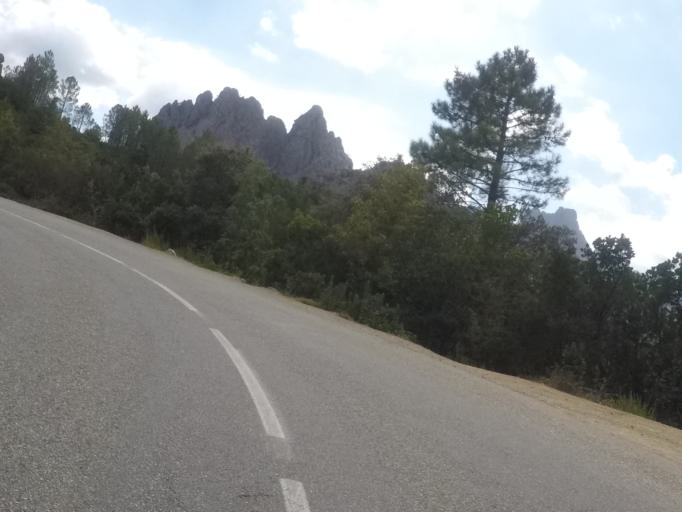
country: FR
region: Corsica
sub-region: Departement de la Corse-du-Sud
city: Sari-Solenzara
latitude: 41.8251
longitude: 9.2721
